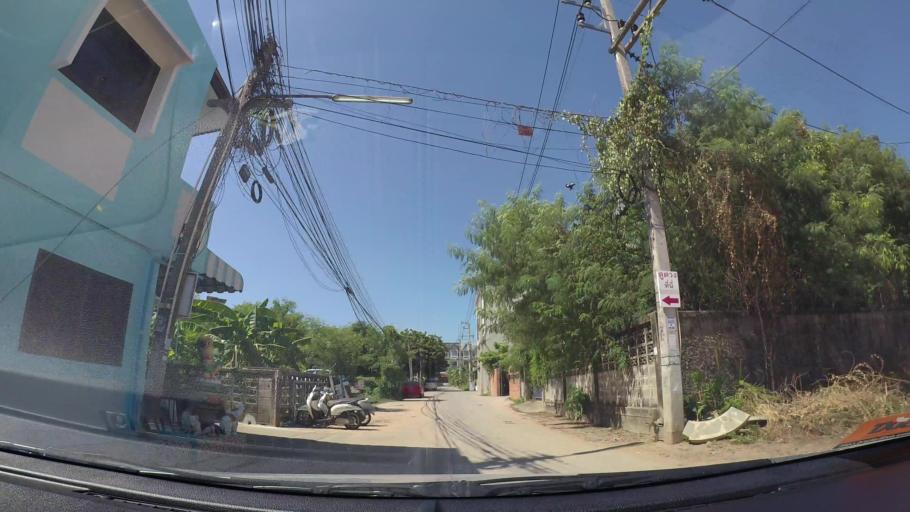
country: TH
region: Chon Buri
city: Si Racha
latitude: 13.1634
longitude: 100.9362
